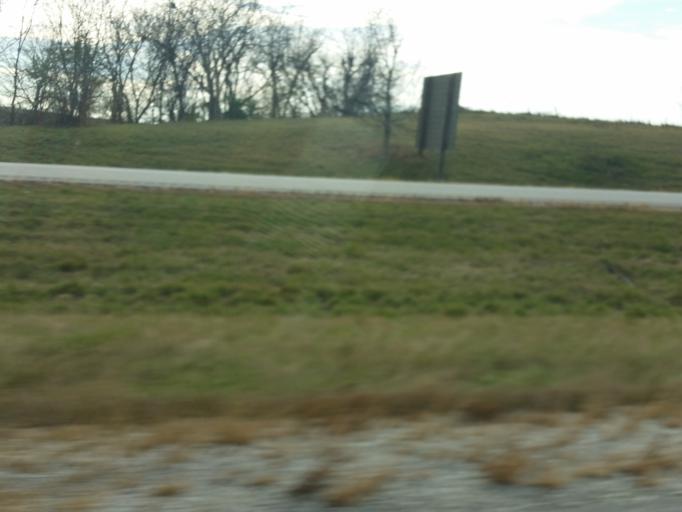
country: US
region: Illinois
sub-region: Henry County
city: Green Rock
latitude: 41.4407
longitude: -90.3425
